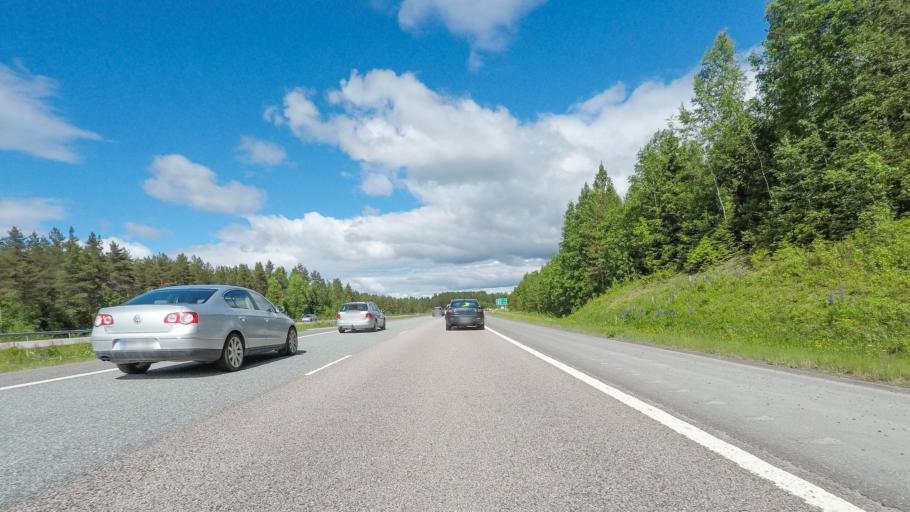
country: FI
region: Paijanne Tavastia
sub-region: Lahti
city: Nastola
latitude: 61.0508
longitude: 25.8538
